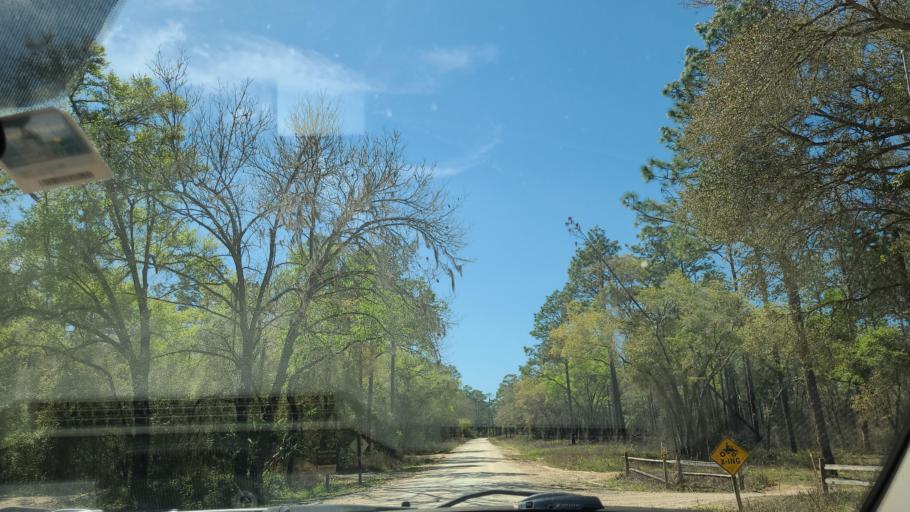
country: US
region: Florida
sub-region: Putnam County
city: Interlachen
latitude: 29.4295
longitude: -81.7885
